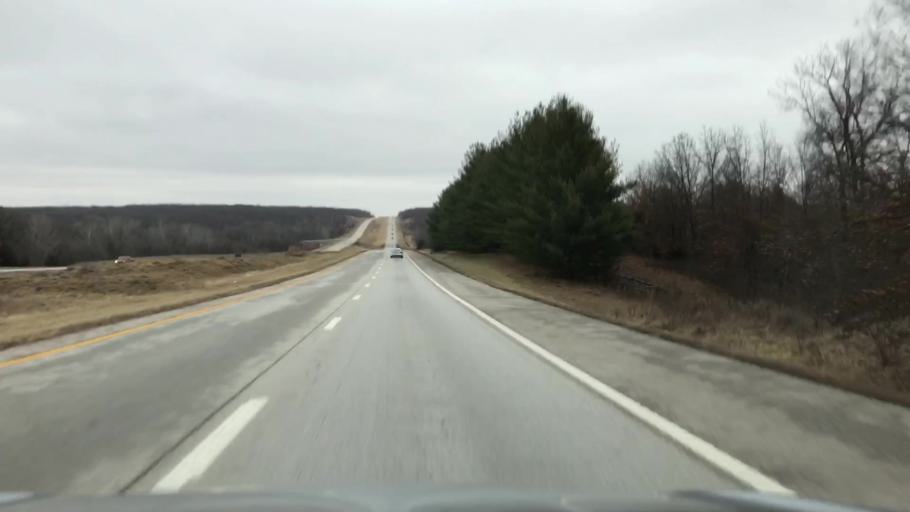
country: US
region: Missouri
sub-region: Linn County
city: Marceline
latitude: 39.7590
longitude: -92.8644
